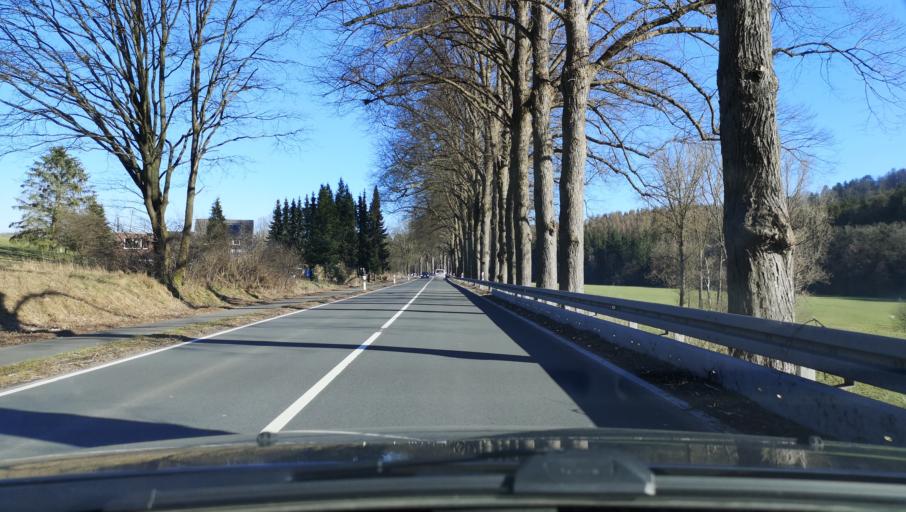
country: DE
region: North Rhine-Westphalia
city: Wipperfurth
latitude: 51.1186
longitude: 7.4233
